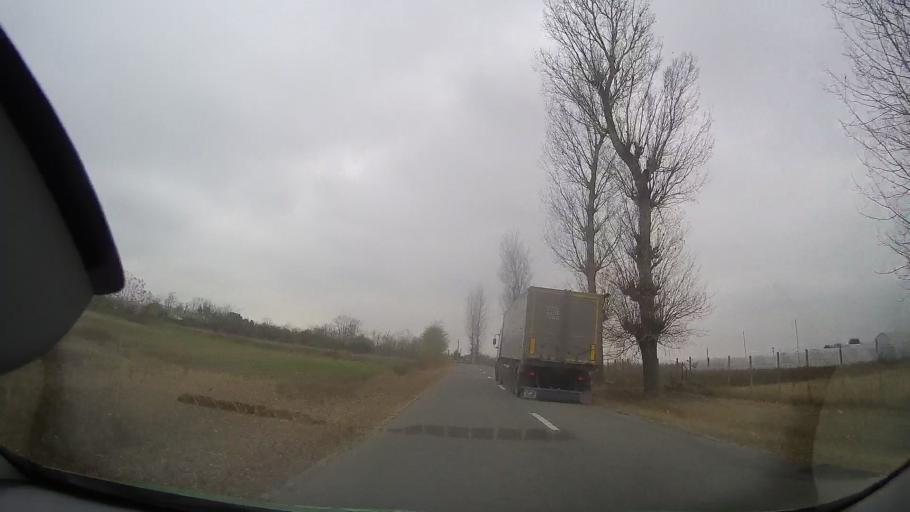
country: RO
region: Ialomita
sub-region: Comuna Valea Macrisului
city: Valea Macrisului
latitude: 44.7392
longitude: 26.8419
